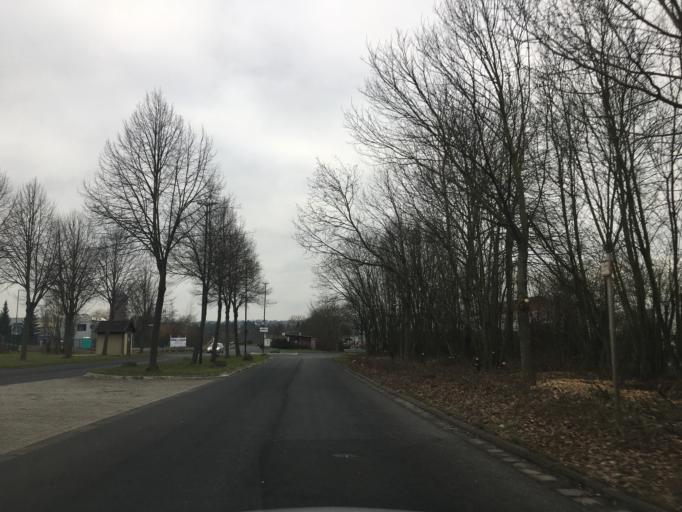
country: DE
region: Hesse
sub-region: Regierungsbezirk Giessen
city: Alsfeld
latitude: 50.7474
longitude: 9.2866
